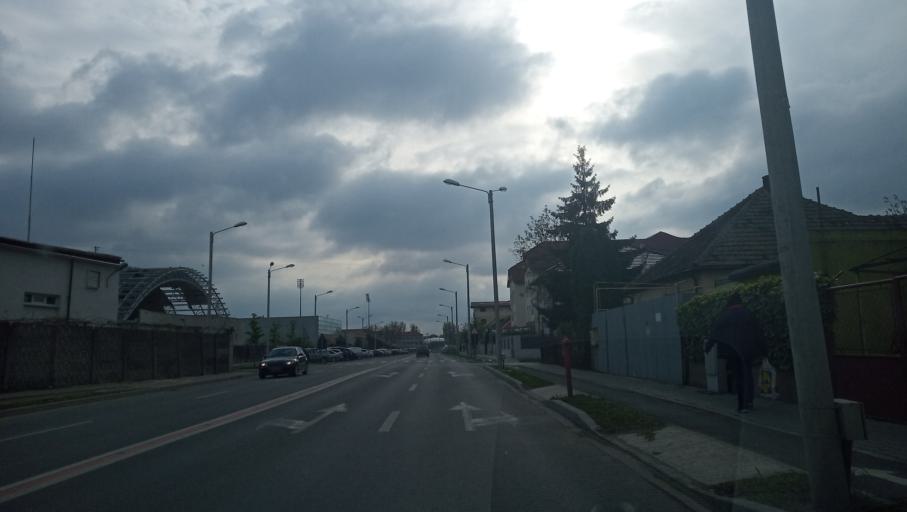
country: RO
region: Timis
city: Timisoara
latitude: 45.7445
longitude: 21.2510
